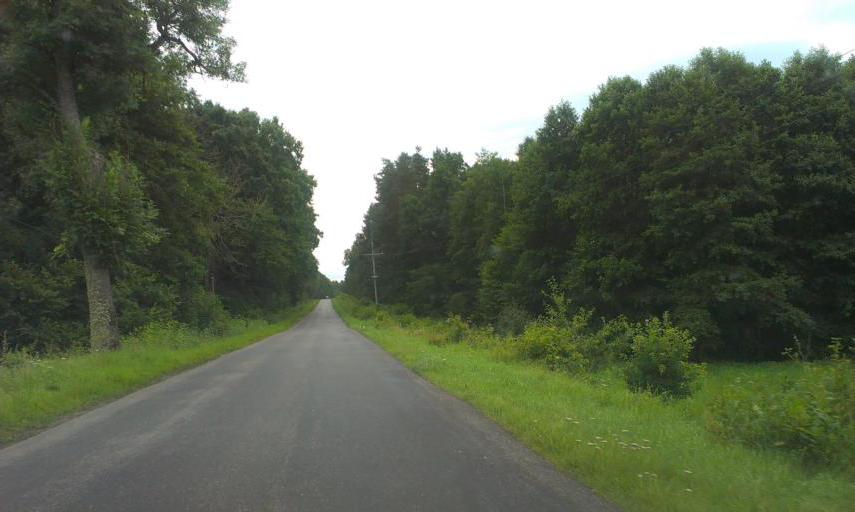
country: PL
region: West Pomeranian Voivodeship
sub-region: Powiat swidwinski
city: Polczyn-Zdroj
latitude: 53.7893
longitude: 16.1384
